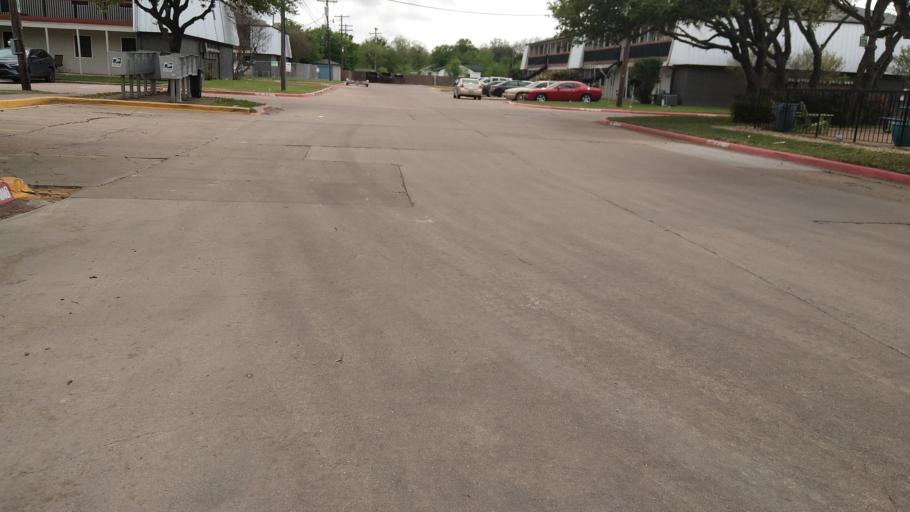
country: US
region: Texas
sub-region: McLennan County
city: Beverly
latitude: 31.5242
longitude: -97.1238
